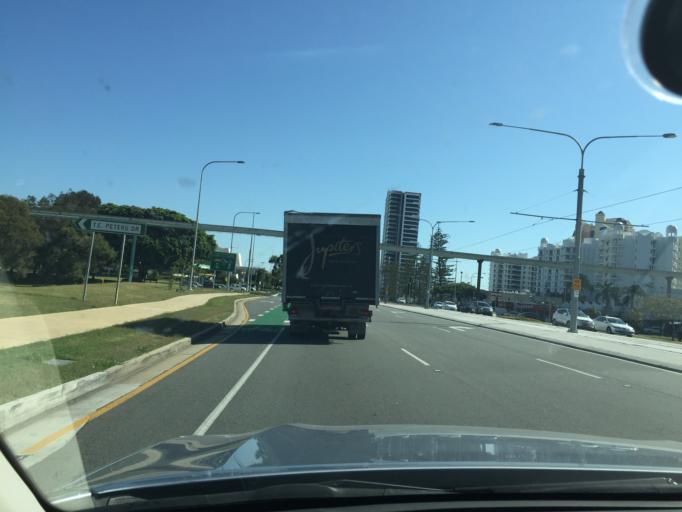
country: AU
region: Queensland
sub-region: Gold Coast
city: Surfers Paradise
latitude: -28.0308
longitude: 153.4302
